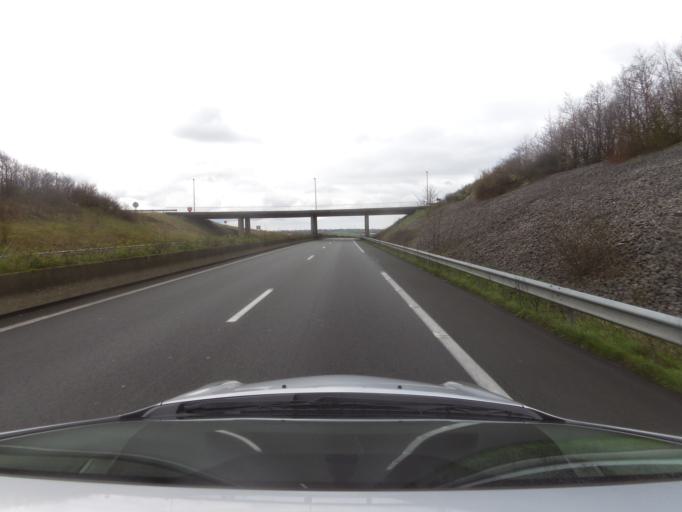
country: FR
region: Nord-Pas-de-Calais
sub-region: Departement du Pas-de-Calais
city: Wimille
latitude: 50.7714
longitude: 1.6494
